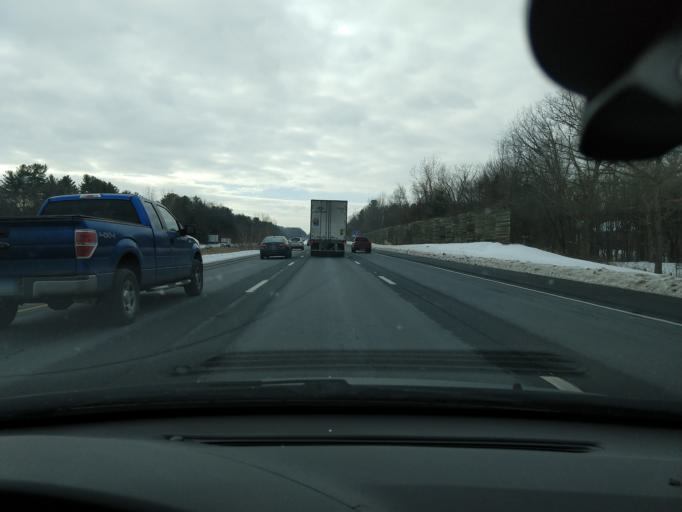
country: US
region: Connecticut
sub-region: Hartford County
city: Plainville
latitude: 41.6475
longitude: -72.8597
